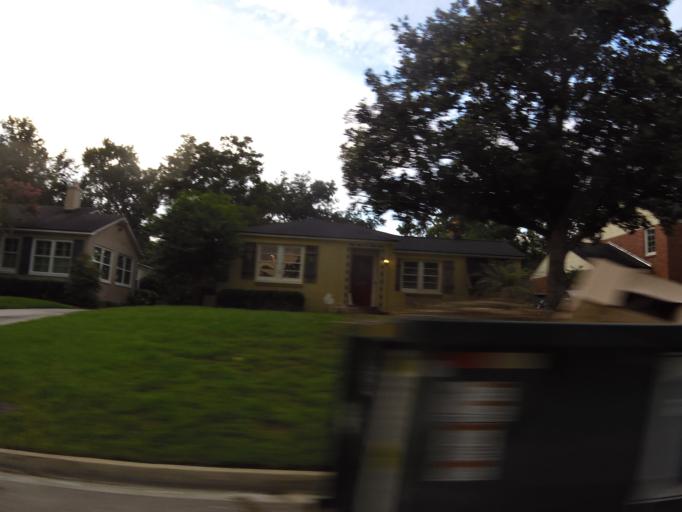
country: US
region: Florida
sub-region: Duval County
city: Jacksonville
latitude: 30.3003
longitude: -81.6485
